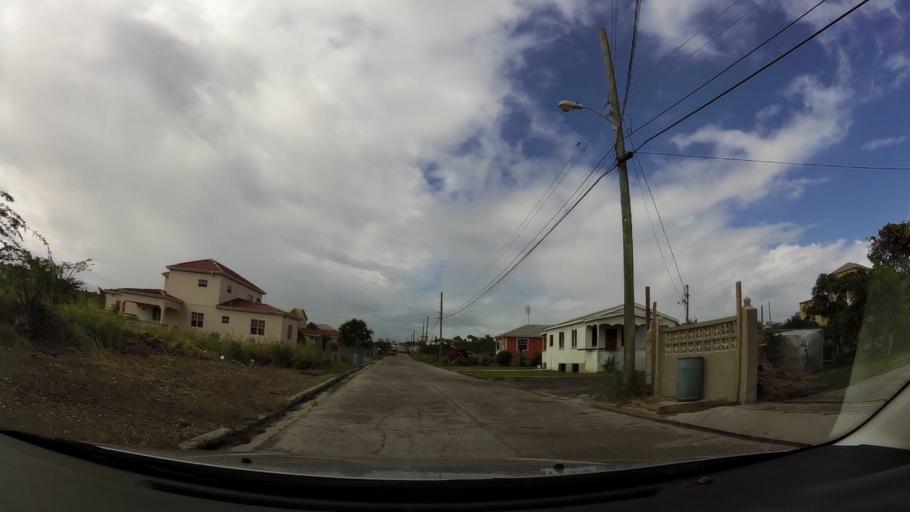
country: AG
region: Saint George
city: Piggotts
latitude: 17.1064
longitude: -61.8084
